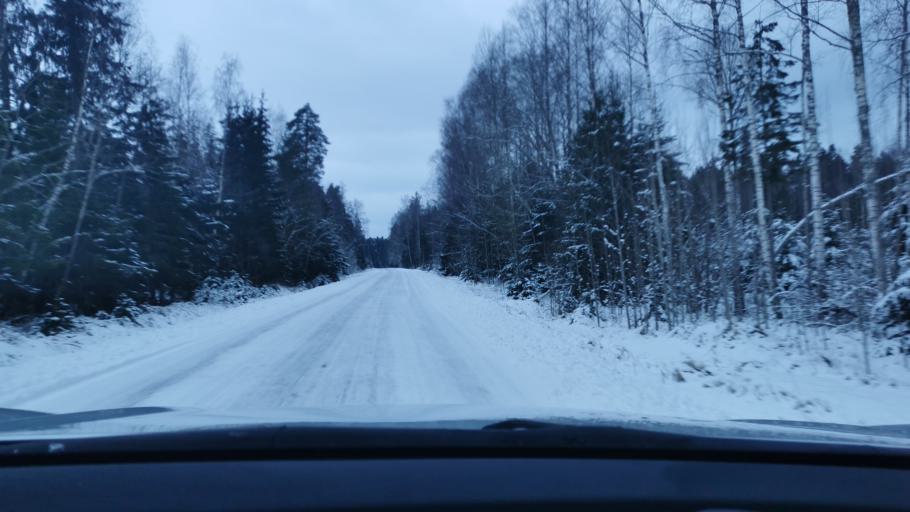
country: EE
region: Laeaene-Virumaa
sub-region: Haljala vald
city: Haljala
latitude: 59.5522
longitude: 26.3593
